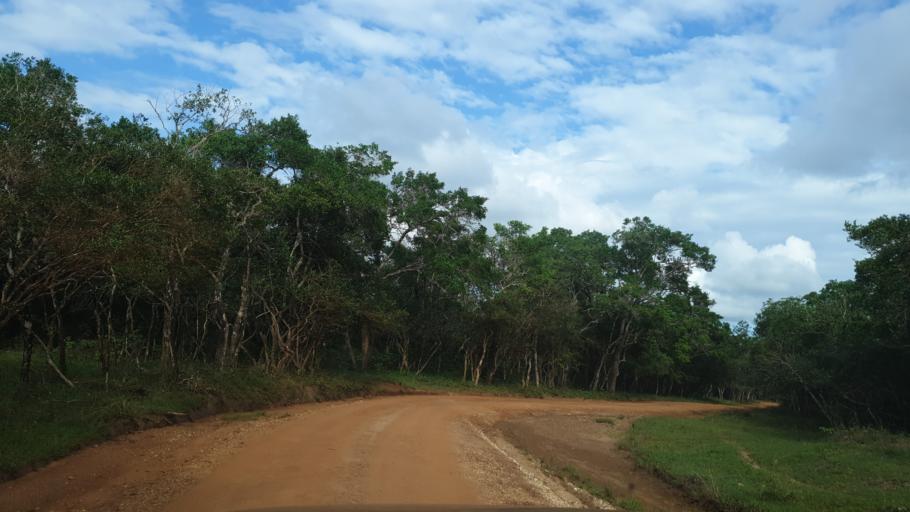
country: LK
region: North Central
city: Anuradhapura
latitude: 8.3633
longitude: 80.0967
